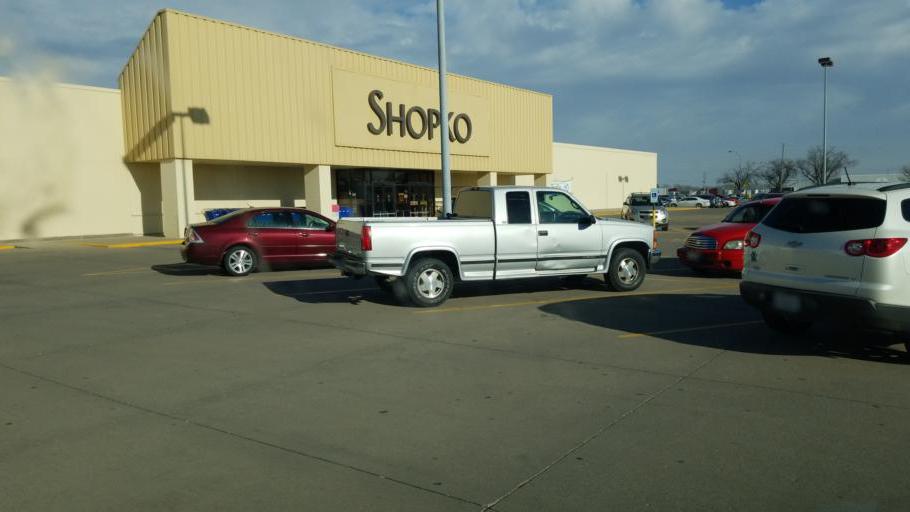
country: US
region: Illinois
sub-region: Warren County
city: Monmouth
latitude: 40.9259
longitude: -90.6424
